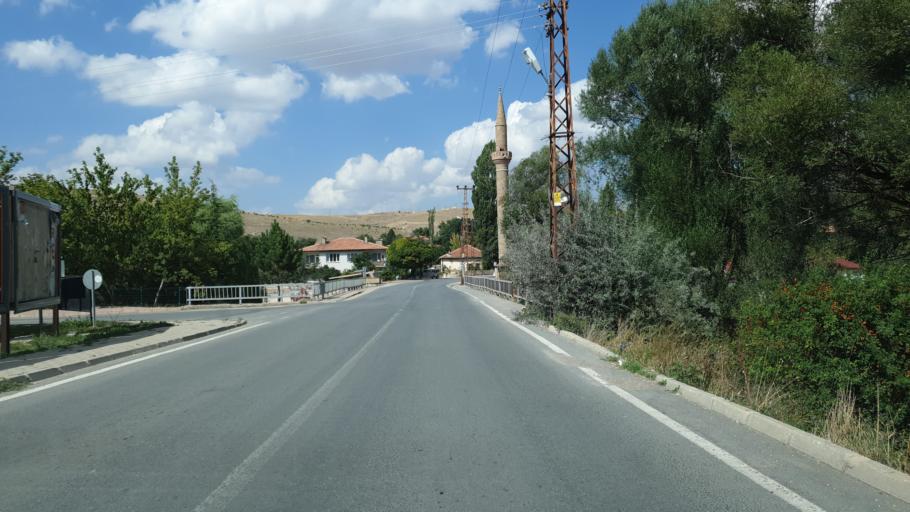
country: TR
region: Kayseri
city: Felahiye
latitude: 39.0924
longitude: 35.5696
